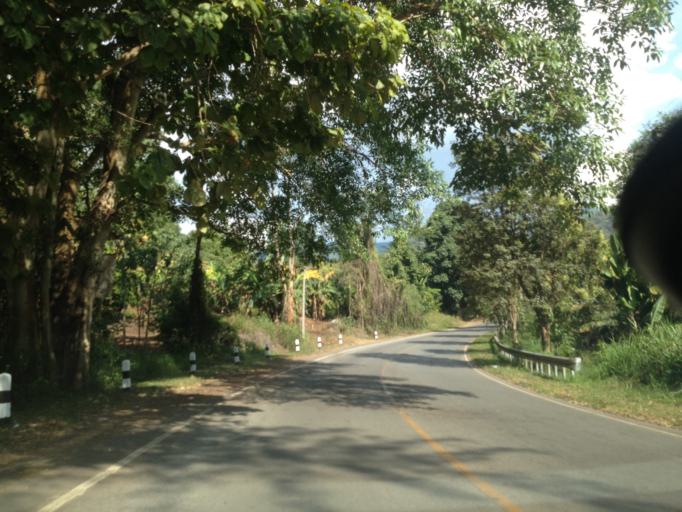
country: TH
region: Chiang Mai
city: Samoeng
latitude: 18.8494
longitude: 98.7393
